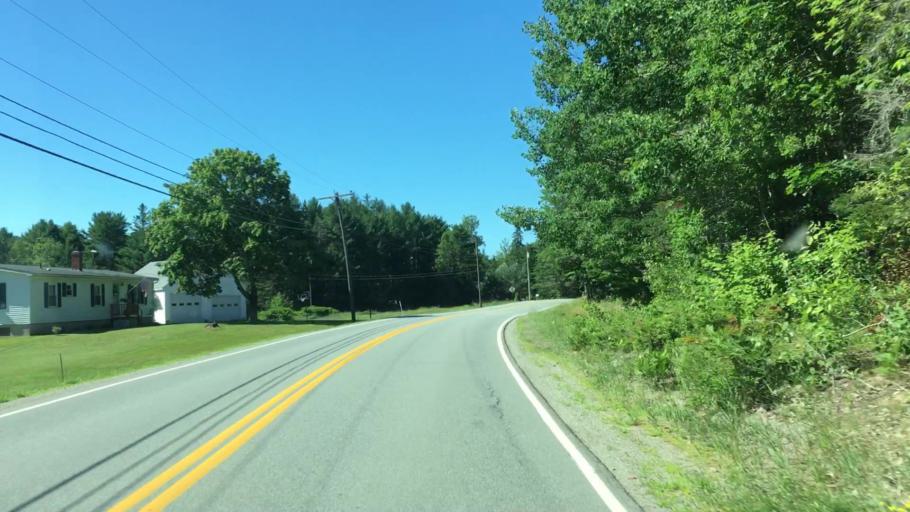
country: US
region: Maine
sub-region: Hancock County
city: Dedham
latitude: 44.7211
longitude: -68.6399
